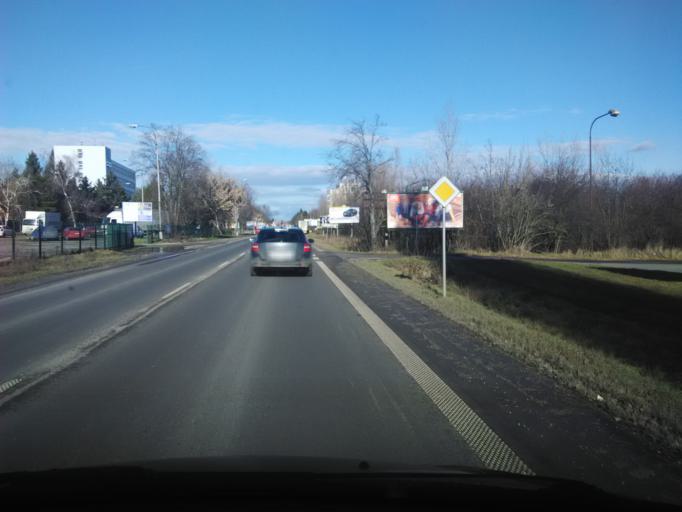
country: SK
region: Nitriansky
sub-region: Okres Nitra
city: Nitra
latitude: 48.2649
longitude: 18.1035
